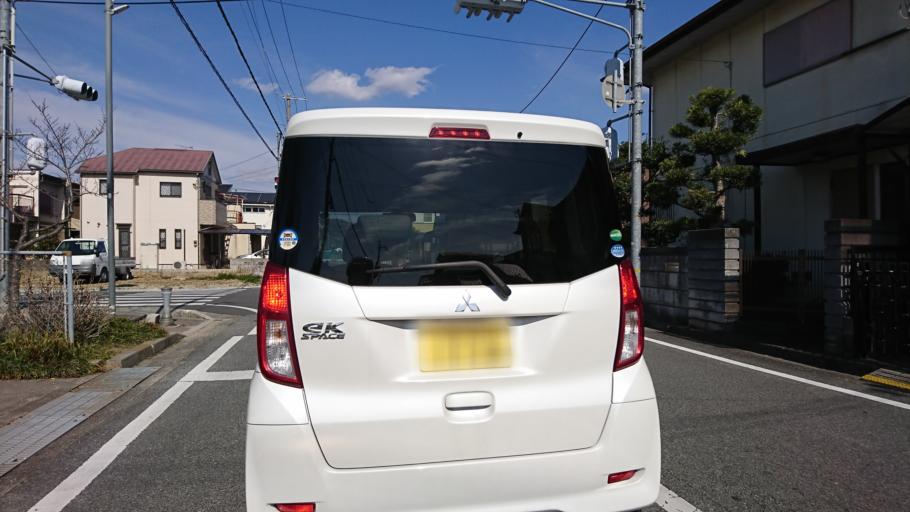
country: JP
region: Hyogo
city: Kakogawacho-honmachi
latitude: 34.7879
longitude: 134.8249
